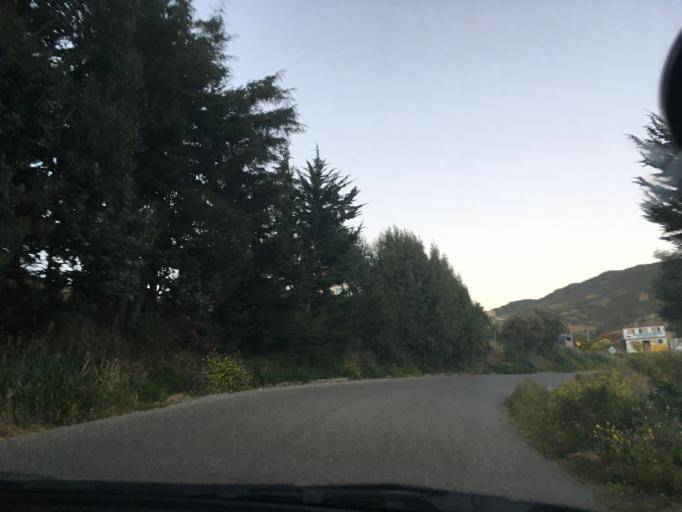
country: CO
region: Boyaca
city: Aquitania
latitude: 5.6173
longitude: -72.9066
